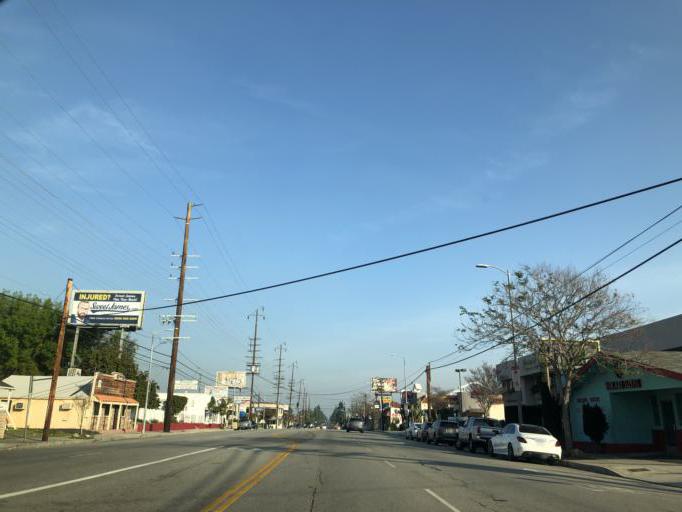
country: US
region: California
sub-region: Los Angeles County
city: Chatsworth
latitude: 34.2572
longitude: -118.5952
